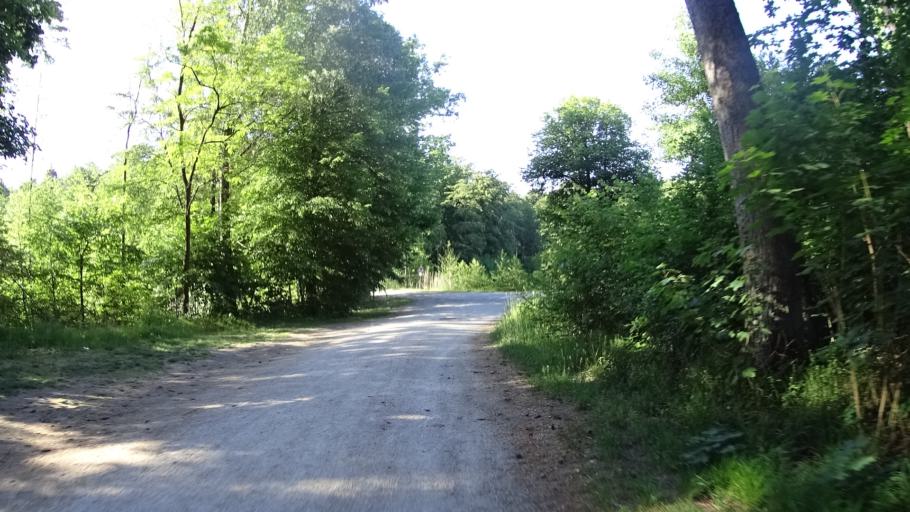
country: DE
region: Bavaria
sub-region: Regierungsbezirk Mittelfranken
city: Lichtenau
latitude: 49.1512
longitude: 10.3926
